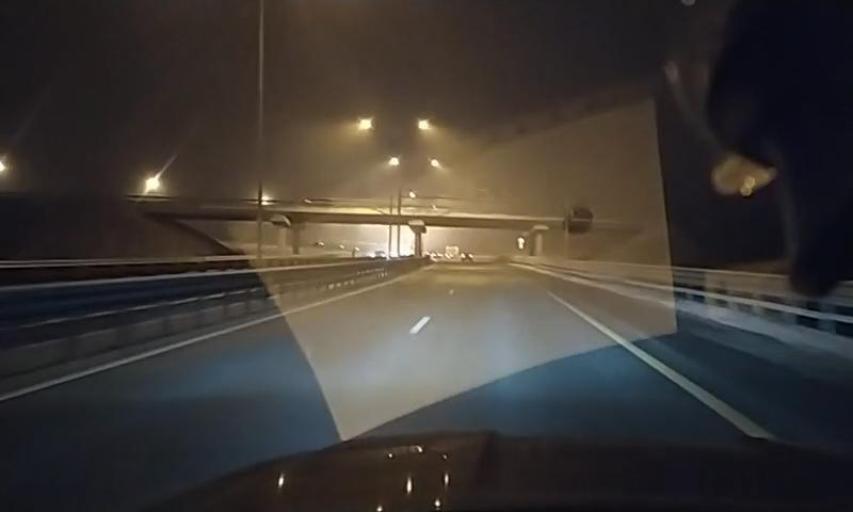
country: RU
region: Leningrad
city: Bugry
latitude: 60.1002
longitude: 30.3839
